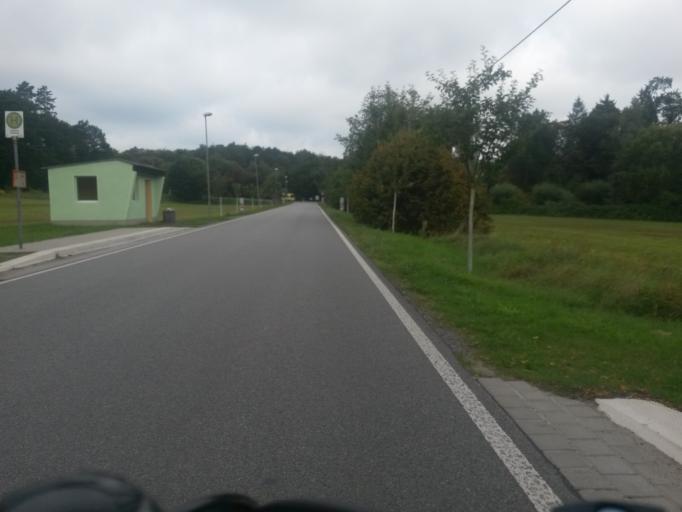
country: DE
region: Brandenburg
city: Angermunde
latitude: 53.0522
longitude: 13.9439
